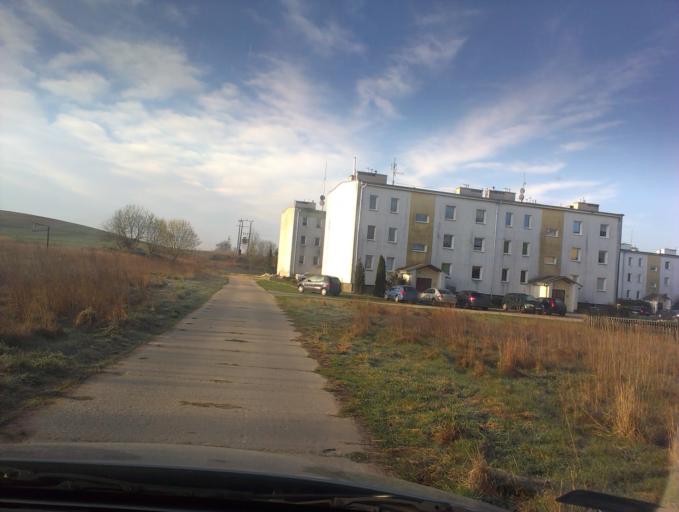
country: PL
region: West Pomeranian Voivodeship
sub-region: Powiat szczecinecki
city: Szczecinek
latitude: 53.7489
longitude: 16.6481
